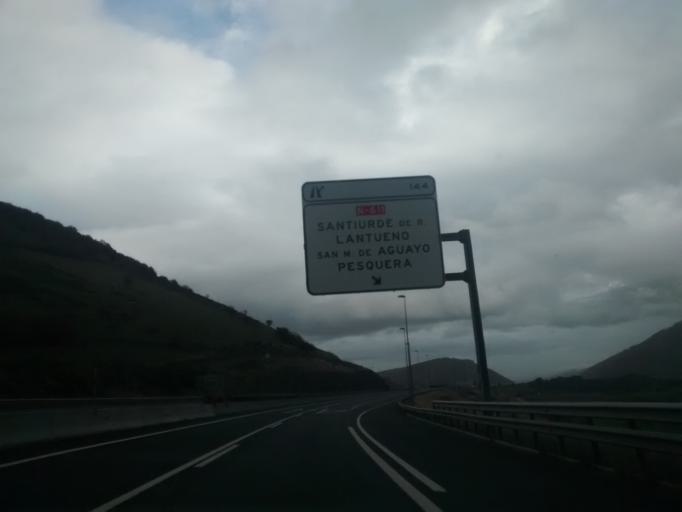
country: ES
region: Cantabria
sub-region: Provincia de Cantabria
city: Santiurde de Reinosa
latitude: 43.0622
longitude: -4.0902
